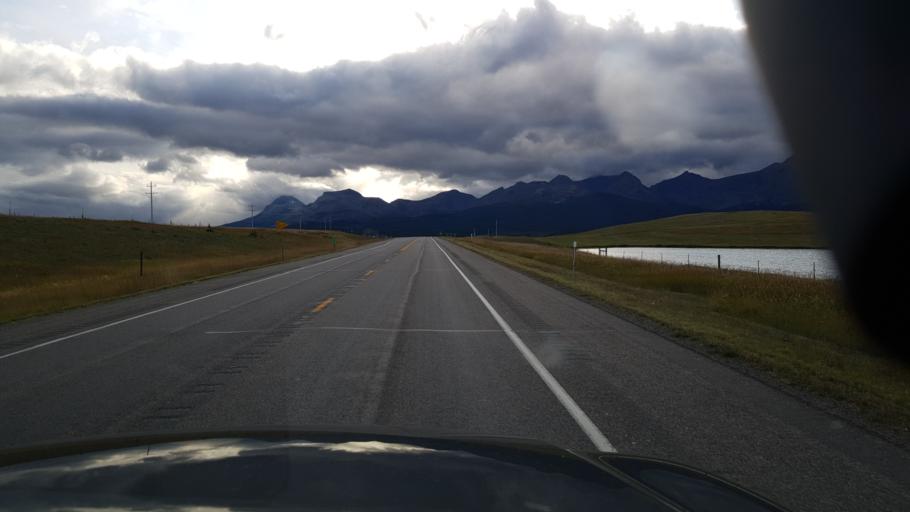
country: US
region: Montana
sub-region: Glacier County
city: South Browning
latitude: 48.4546
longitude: -113.1887
